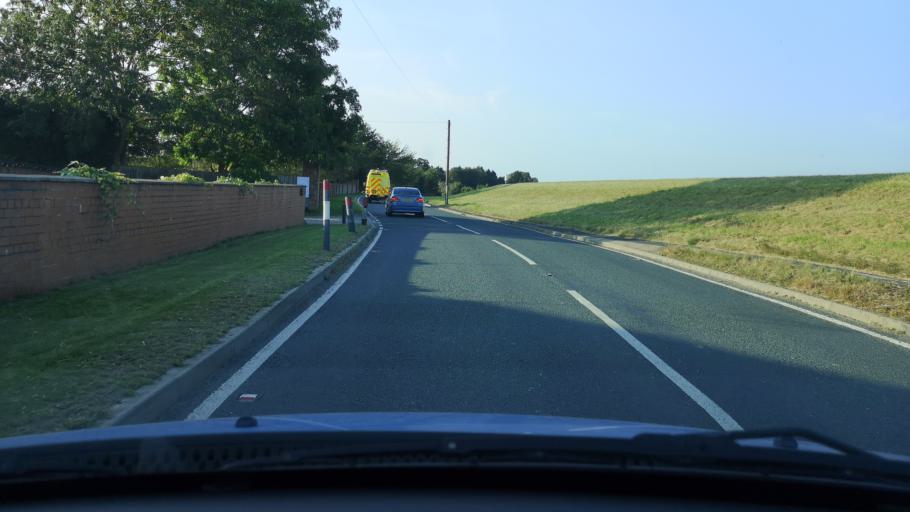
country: GB
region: England
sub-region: East Riding of Yorkshire
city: Goole
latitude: 53.6853
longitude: -0.8592
